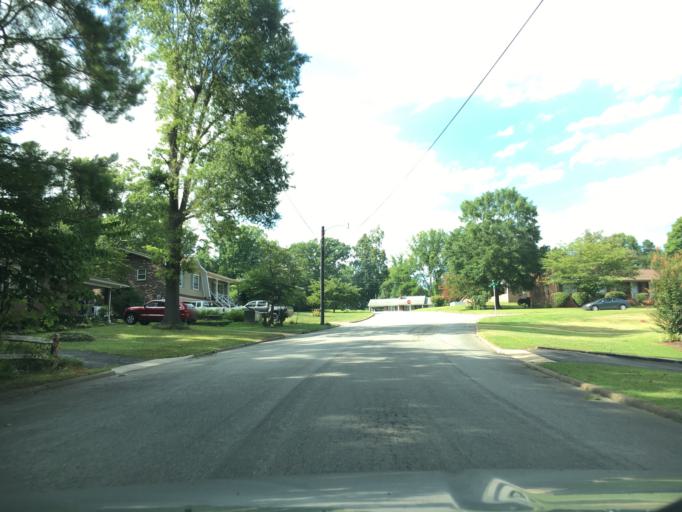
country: US
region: Virginia
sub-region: Halifax County
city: South Boston
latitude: 36.7112
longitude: -78.9097
